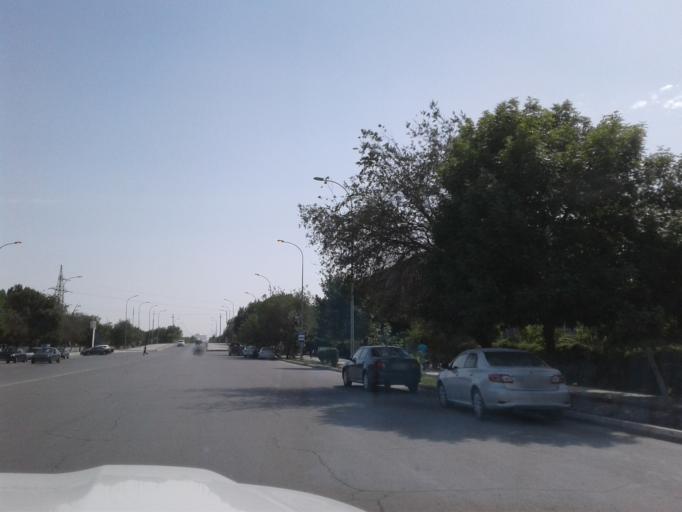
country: TM
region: Dasoguz
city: Dasoguz
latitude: 41.8417
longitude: 59.9699
